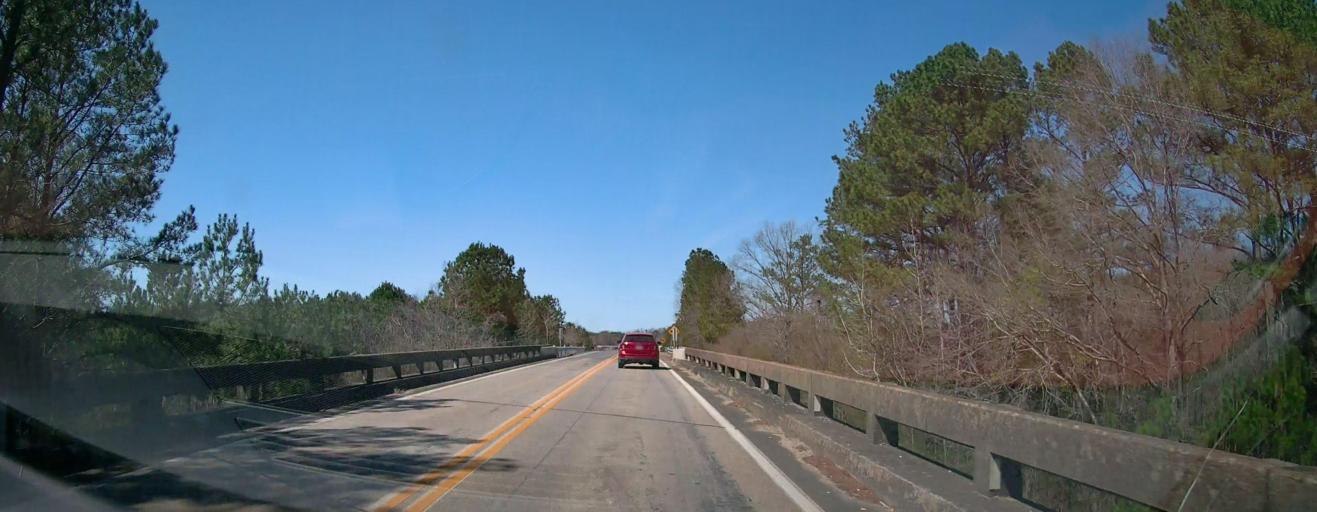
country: US
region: Alabama
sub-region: Calhoun County
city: Ohatchee
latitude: 33.7819
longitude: -86.0078
